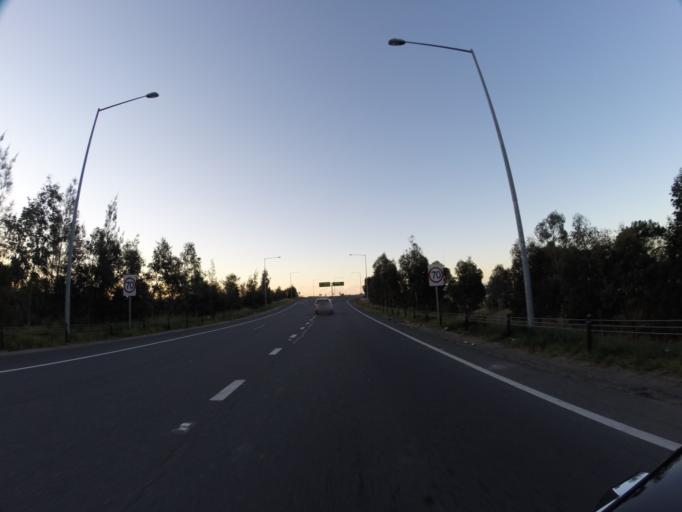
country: AU
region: New South Wales
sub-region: Campbelltown Municipality
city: Glenfield
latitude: -33.9559
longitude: 150.8759
